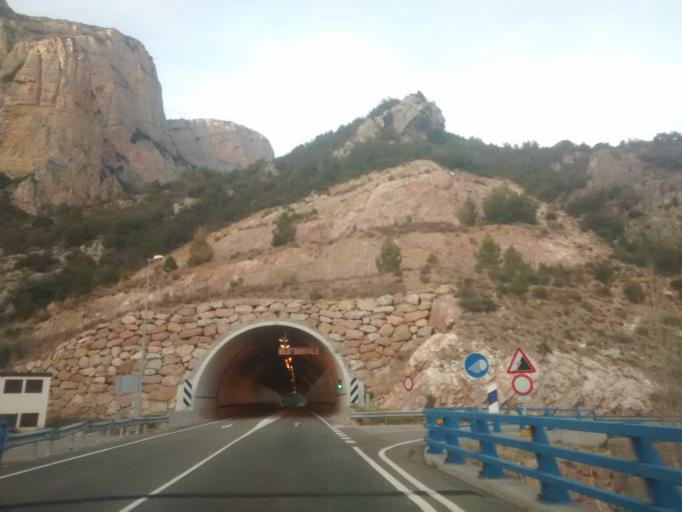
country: ES
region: Catalonia
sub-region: Provincia de Lleida
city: Oliana
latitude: 42.1175
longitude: 1.3038
